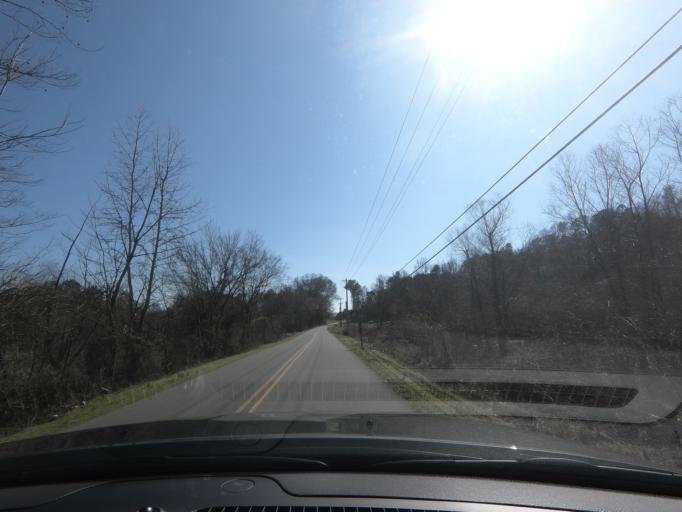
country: US
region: Georgia
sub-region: Bartow County
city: Rydal
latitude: 34.4432
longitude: -84.8083
